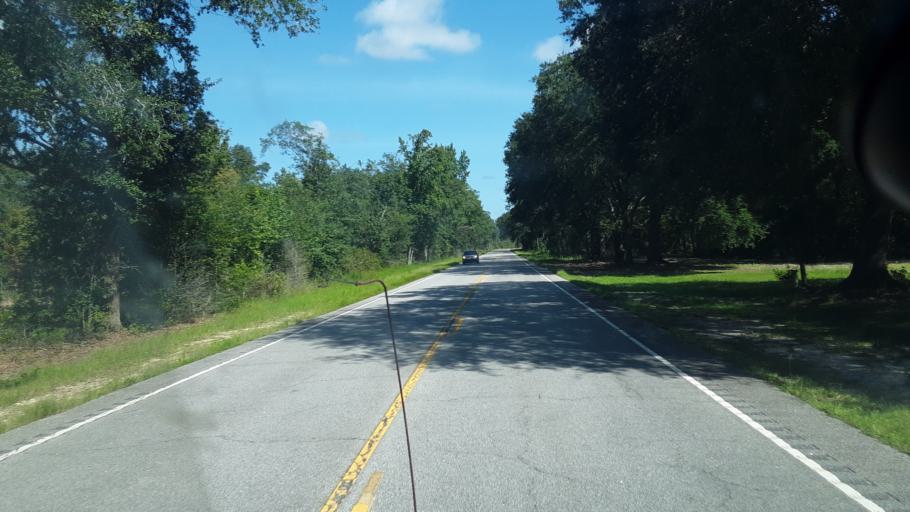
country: US
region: South Carolina
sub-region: Hampton County
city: Varnville
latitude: 32.7867
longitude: -81.0583
